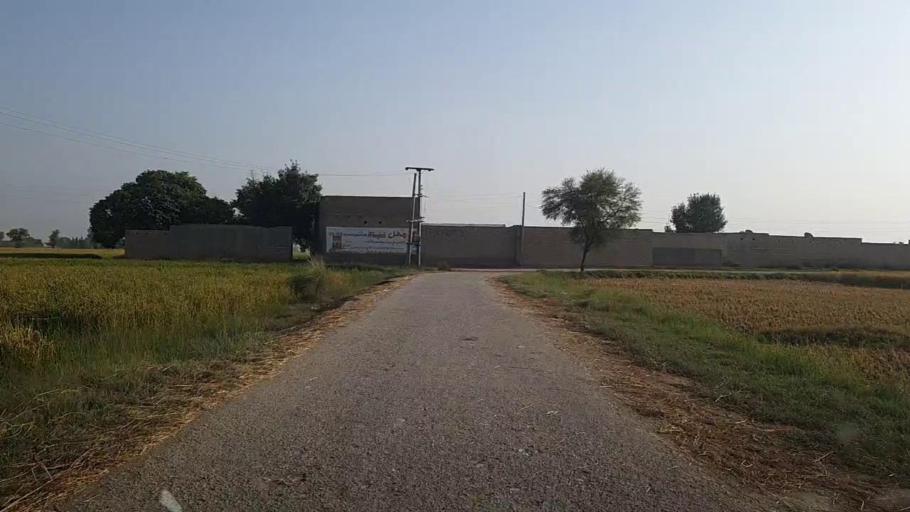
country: PK
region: Sindh
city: Kandhkot
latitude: 28.2517
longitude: 69.1602
